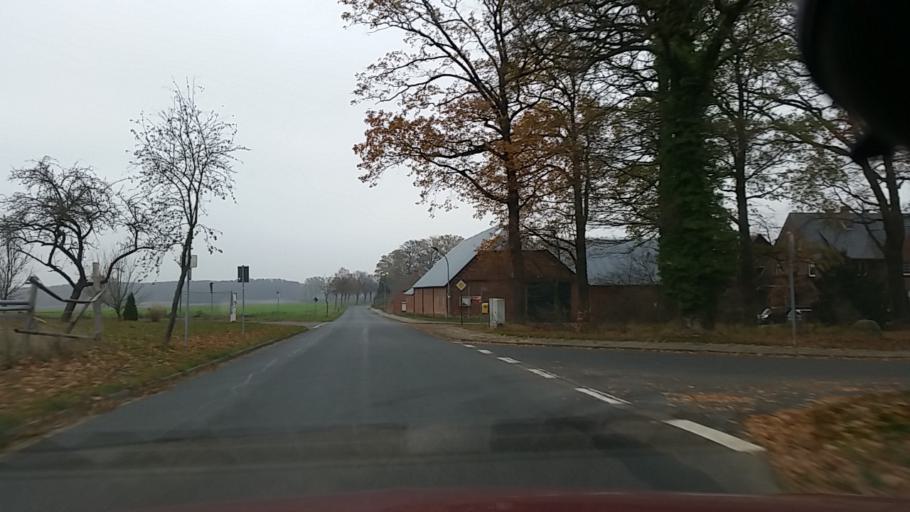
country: DE
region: Lower Saxony
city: Stadensen
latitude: 52.8486
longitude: 10.5640
